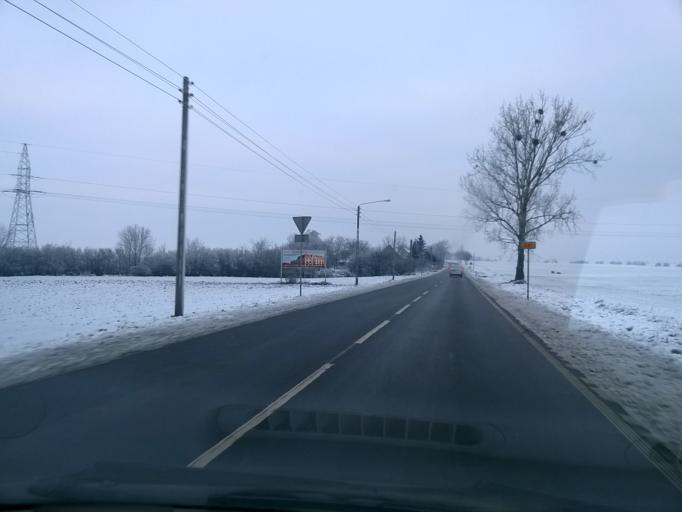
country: PL
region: Kujawsko-Pomorskie
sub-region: Powiat nakielski
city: Naklo nad Notecia
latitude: 53.1528
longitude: 17.5909
